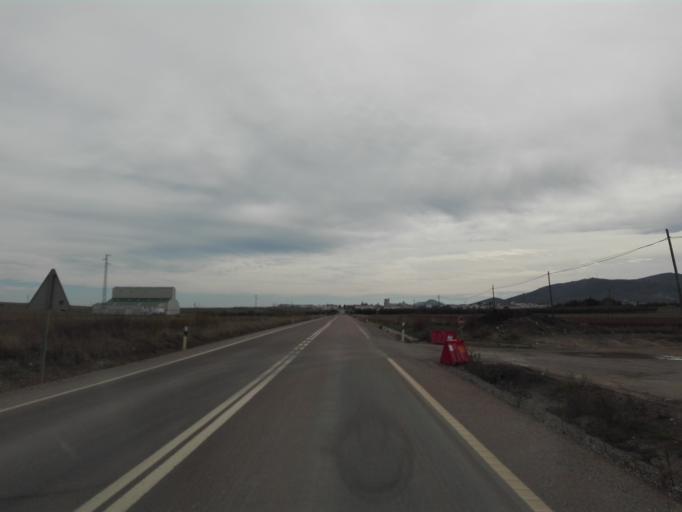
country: ES
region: Extremadura
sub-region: Provincia de Badajoz
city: Llerena
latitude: 38.2532
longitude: -6.0282
